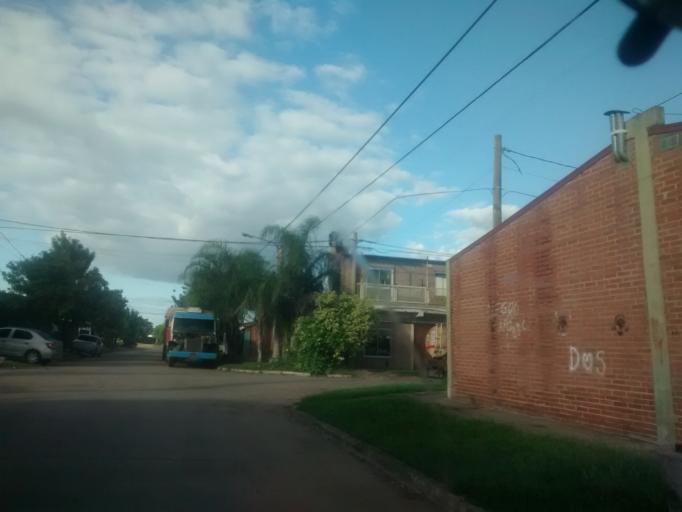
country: AR
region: Chaco
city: Fontana
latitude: -27.4516
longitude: -59.0255
